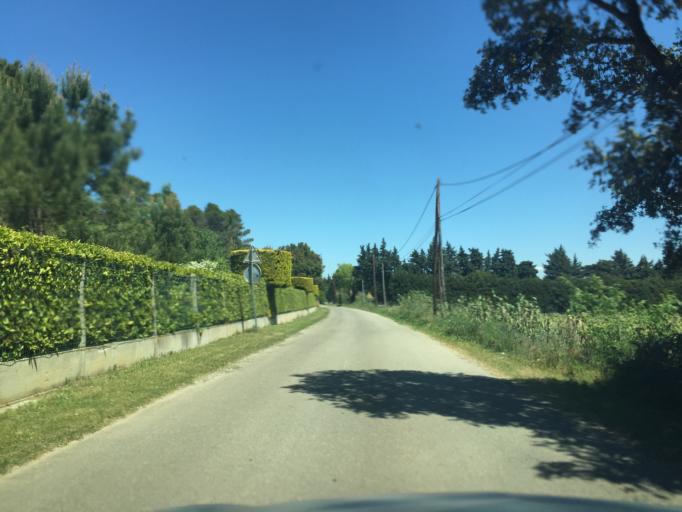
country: FR
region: Provence-Alpes-Cote d'Azur
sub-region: Departement du Vaucluse
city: Orange
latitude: 44.1066
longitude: 4.7993
